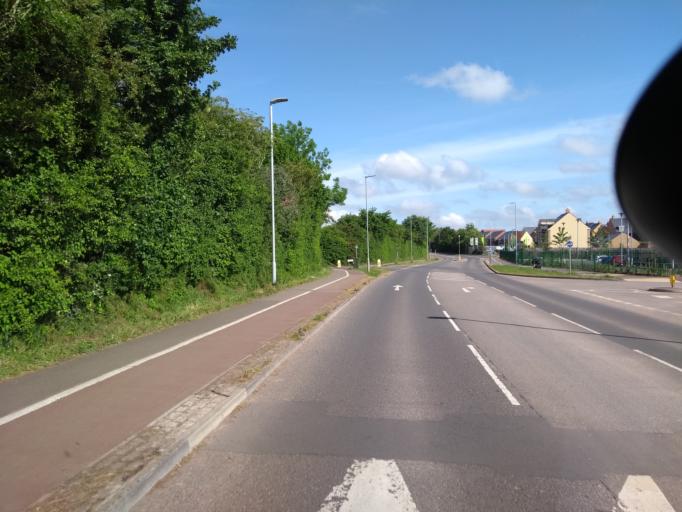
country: GB
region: England
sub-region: Somerset
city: Taunton
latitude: 51.0318
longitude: -3.0818
